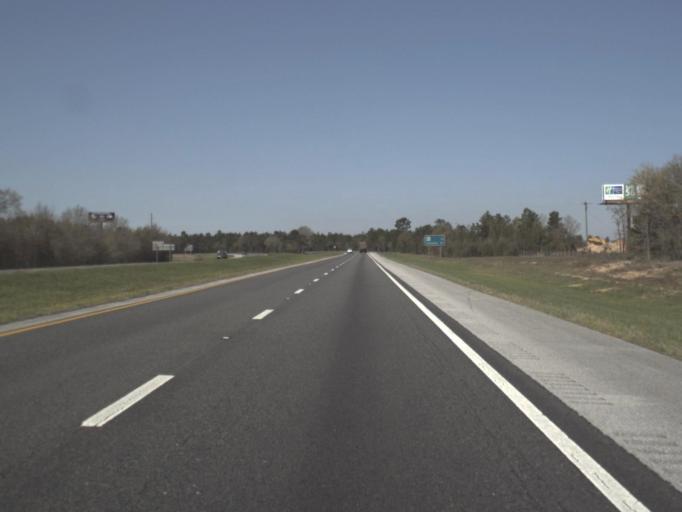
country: US
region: Florida
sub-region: Okaloosa County
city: Crestview
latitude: 30.7335
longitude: -86.3658
